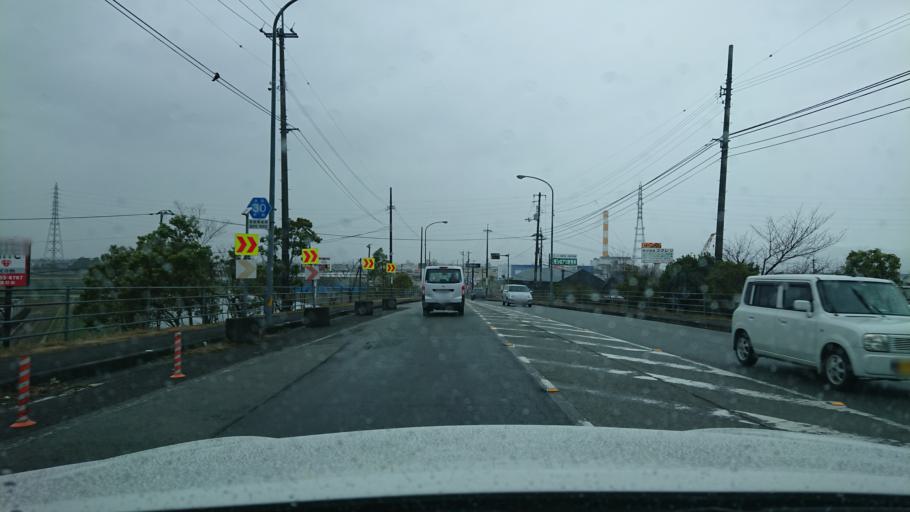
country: JP
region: Tokushima
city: Ishii
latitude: 34.0831
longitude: 134.5002
